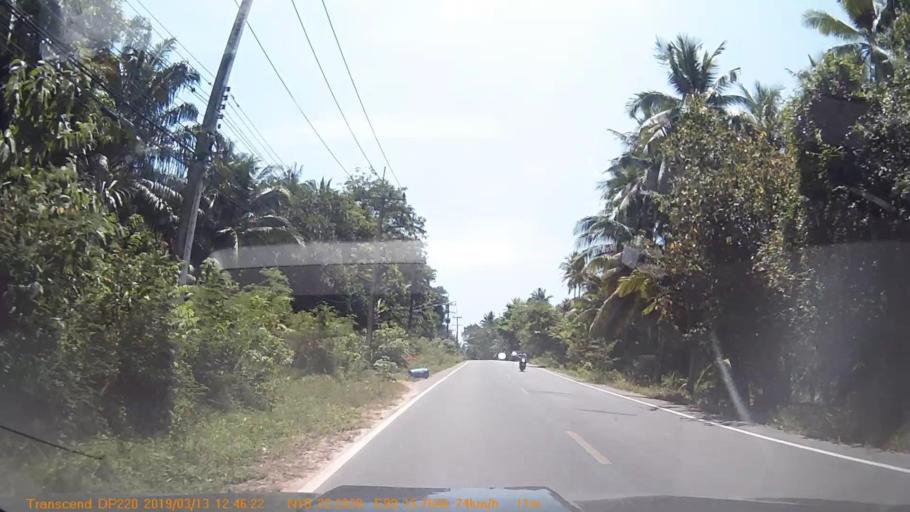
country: TH
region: Chumphon
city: Chumphon
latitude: 10.3711
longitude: 99.2627
